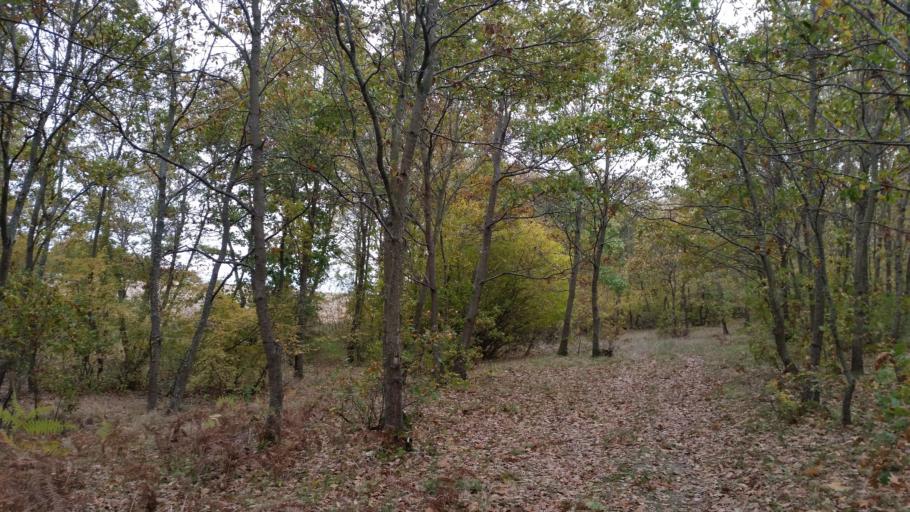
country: TR
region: Tekirdag
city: Cerkezkoey
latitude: 41.3735
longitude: 28.0018
